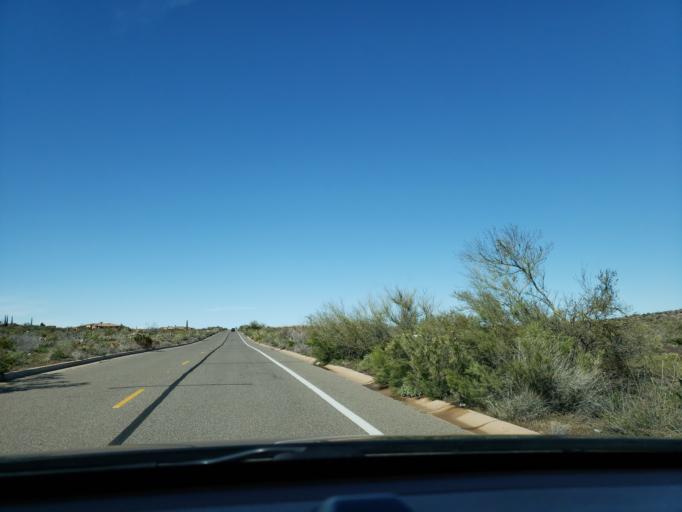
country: US
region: Arizona
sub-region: Maricopa County
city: Carefree
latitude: 33.7186
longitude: -111.8264
